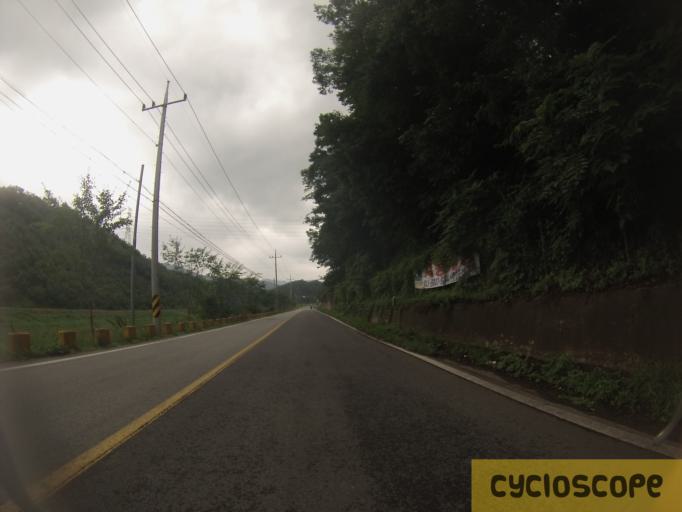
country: KR
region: Chungcheongnam-do
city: Yesan
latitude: 36.5822
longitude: 126.7943
